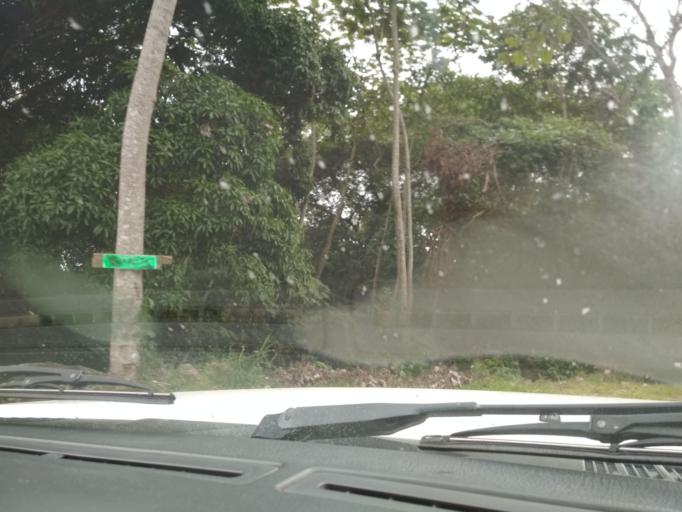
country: MX
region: Veracruz
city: El Castillo
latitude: 19.5656
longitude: -96.8475
